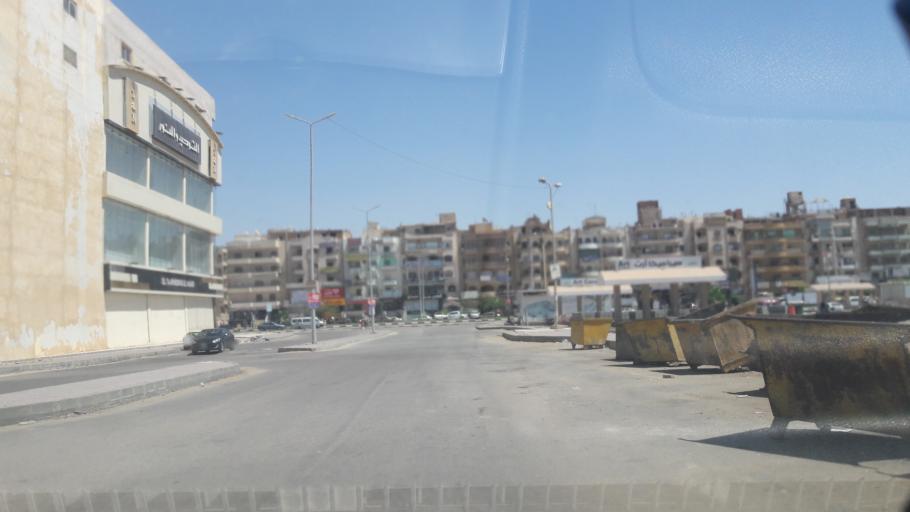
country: EG
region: Al Jizah
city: Madinat Sittah Uktubar
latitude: 29.9693
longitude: 30.9377
